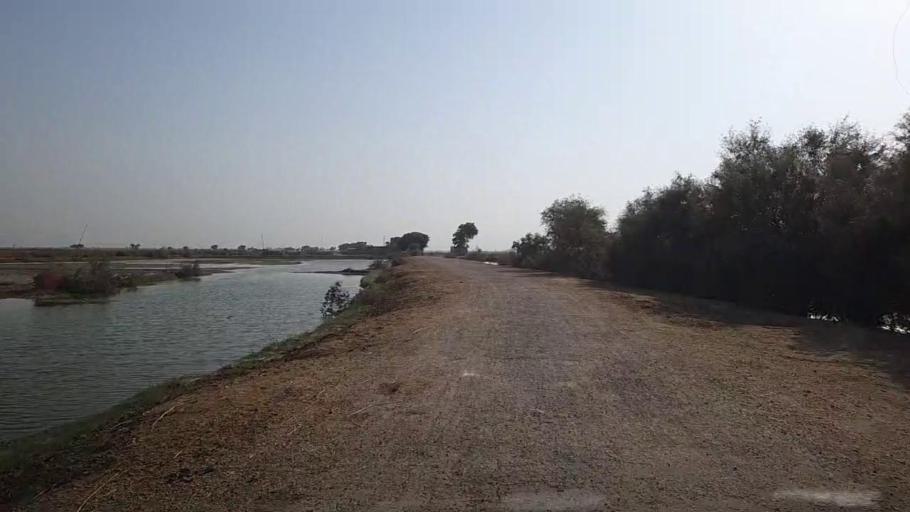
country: PK
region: Sindh
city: Kandhkot
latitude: 28.3802
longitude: 69.3359
